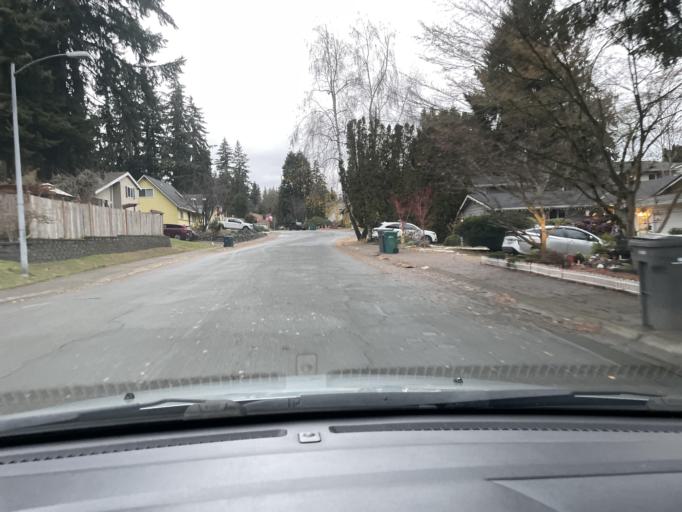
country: US
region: Washington
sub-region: King County
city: Kingsgate
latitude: 47.7227
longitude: -122.1789
